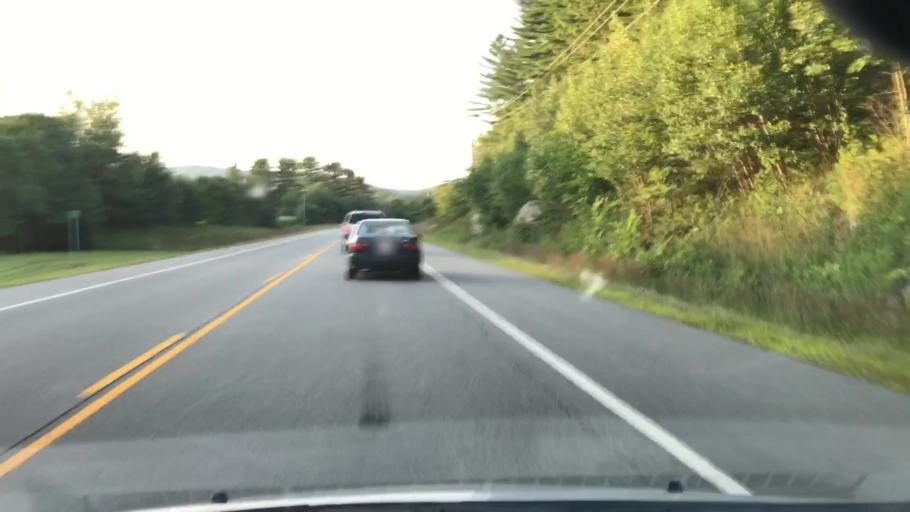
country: US
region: New Hampshire
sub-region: Grafton County
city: Rumney
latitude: 43.8584
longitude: -71.9112
